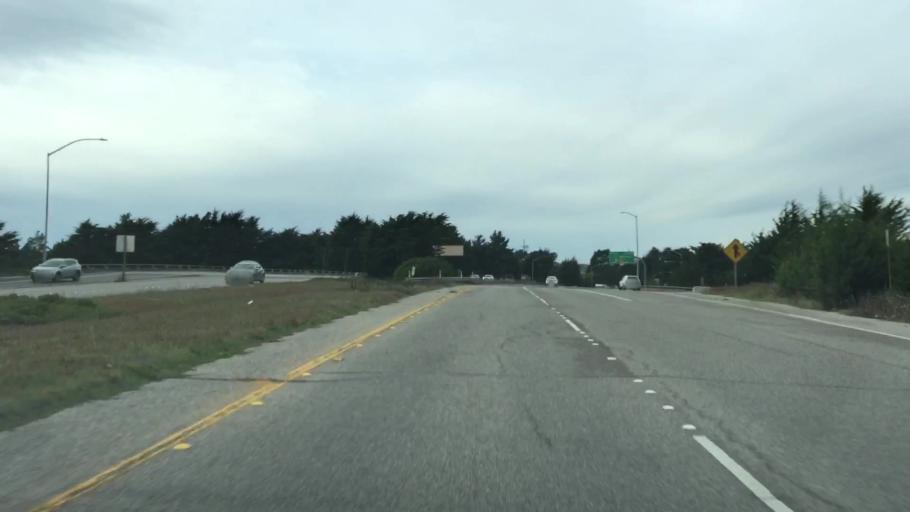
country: US
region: California
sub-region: San Mateo County
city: Broadmoor
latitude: 37.6678
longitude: -122.4838
